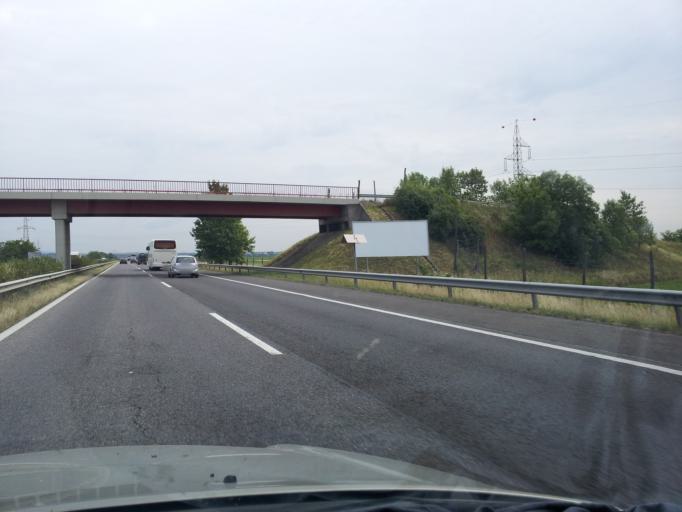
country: HU
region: Heves
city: Hort
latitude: 47.6919
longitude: 19.7518
